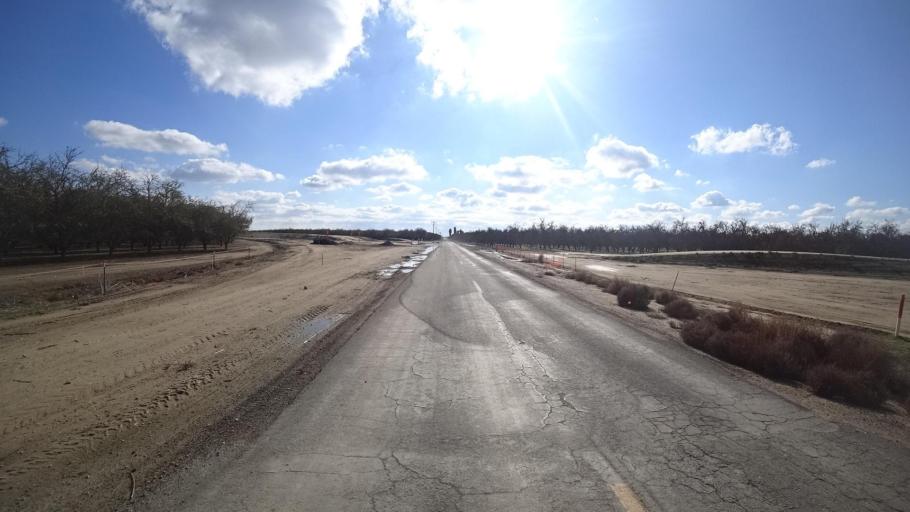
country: US
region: California
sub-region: Kern County
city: Delano
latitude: 35.7239
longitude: -119.3659
